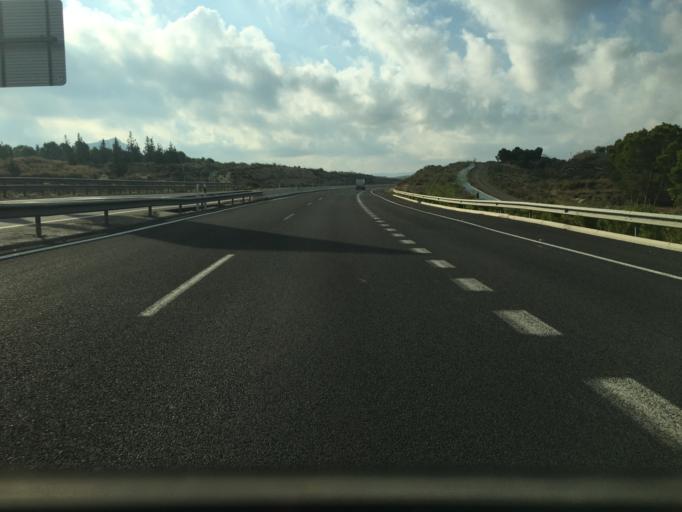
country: ES
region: Murcia
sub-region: Murcia
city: Beniel
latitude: 37.9958
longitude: -0.9809
